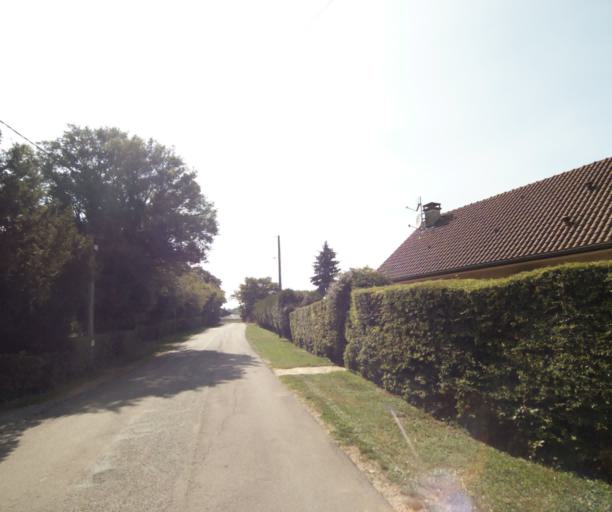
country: FR
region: Bourgogne
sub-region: Departement de Saone-et-Loire
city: Tournus
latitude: 46.5731
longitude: 4.8891
